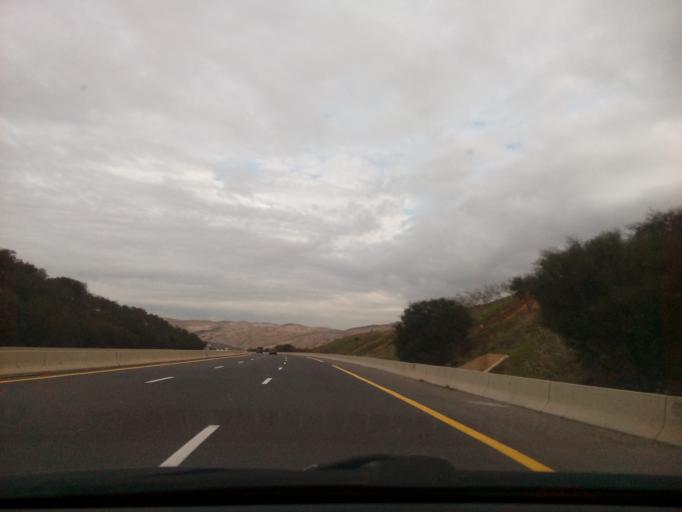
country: DZ
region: Sidi Bel Abbes
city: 'Ain el Berd
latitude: 35.4475
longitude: -0.3999
